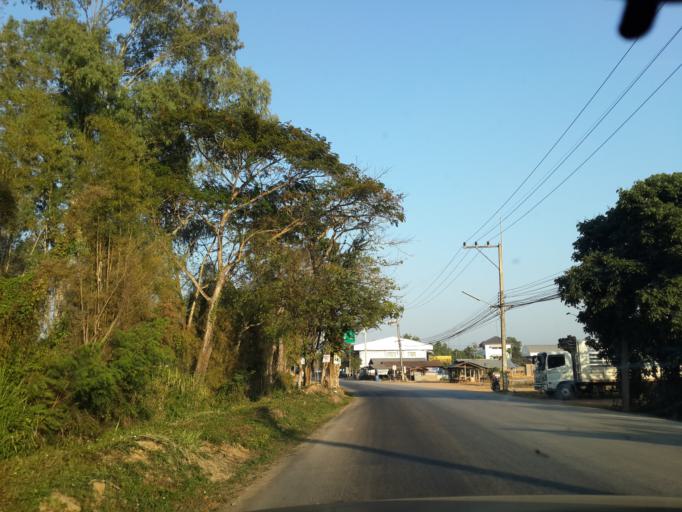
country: TH
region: Chiang Mai
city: Chai Prakan
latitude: 19.8022
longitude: 99.1658
